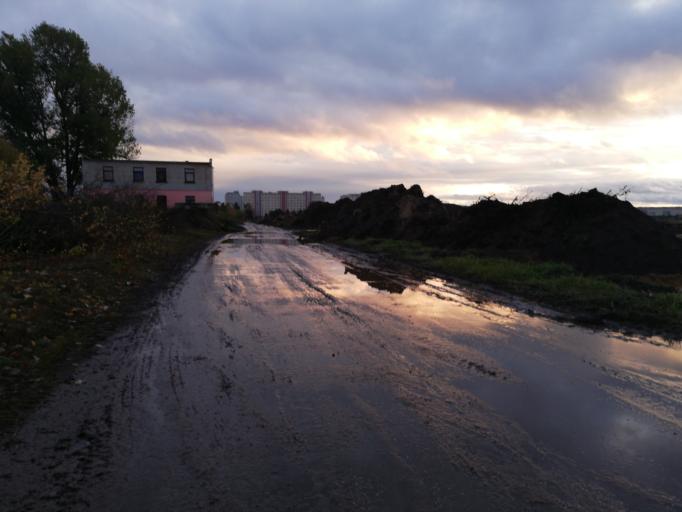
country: LV
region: Stopini
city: Ulbroka
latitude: 56.9519
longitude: 24.2368
